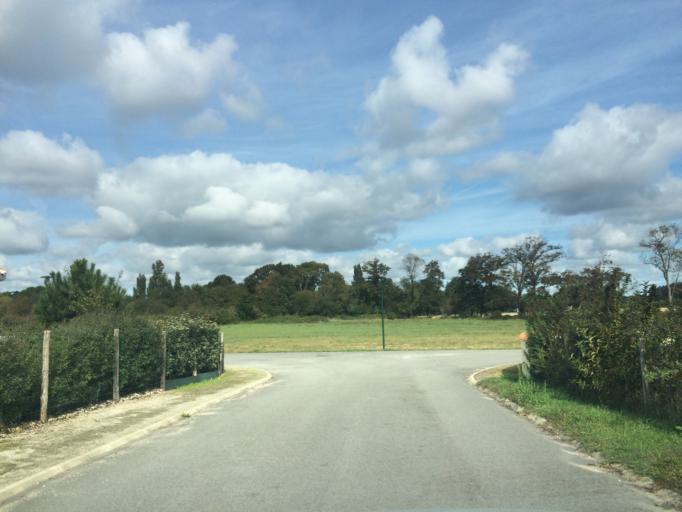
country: FR
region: Pays de la Loire
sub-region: Departement de la Loire-Atlantique
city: Chemere
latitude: 47.1181
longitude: -1.9283
